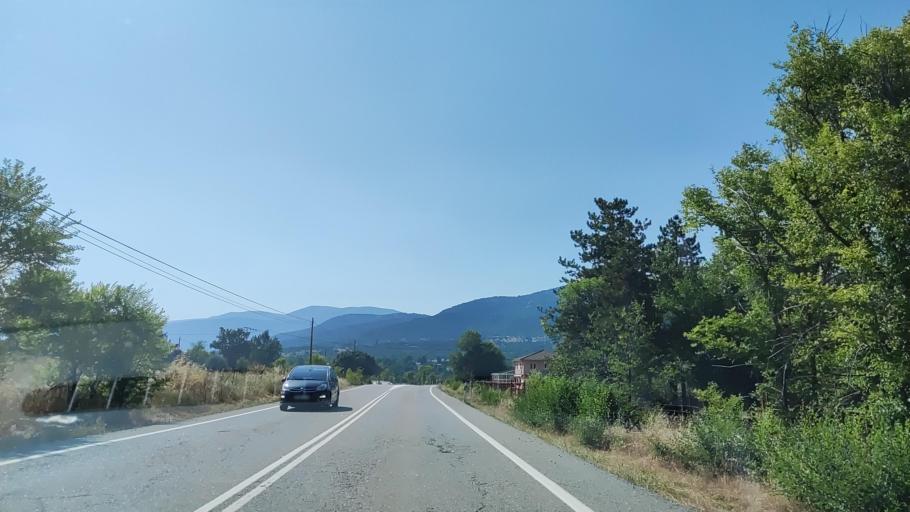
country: ES
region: Madrid
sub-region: Provincia de Madrid
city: Garganta de los Montes
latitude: 40.9425
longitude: -3.7082
